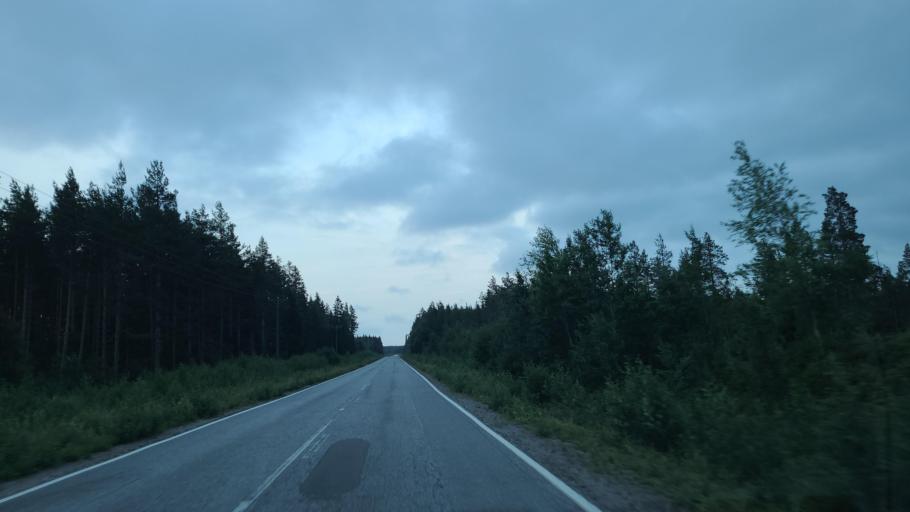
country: FI
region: Ostrobothnia
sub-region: Vaasa
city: Replot
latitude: 63.2281
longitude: 21.2228
